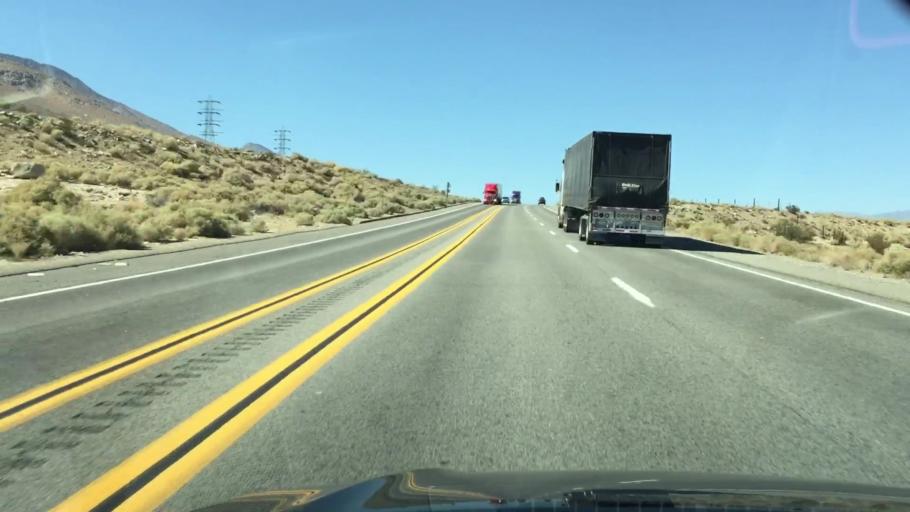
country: US
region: California
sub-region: Inyo County
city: Lone Pine
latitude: 36.3491
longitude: -118.0244
